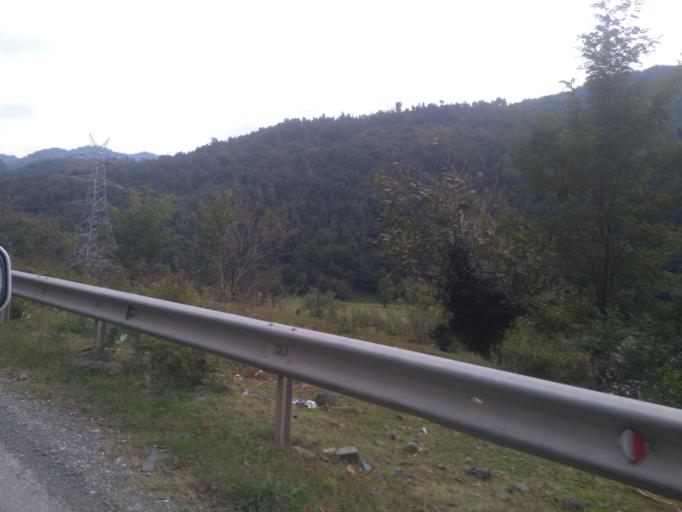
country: TR
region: Artvin
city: Camili
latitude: 41.5570
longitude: 41.8105
